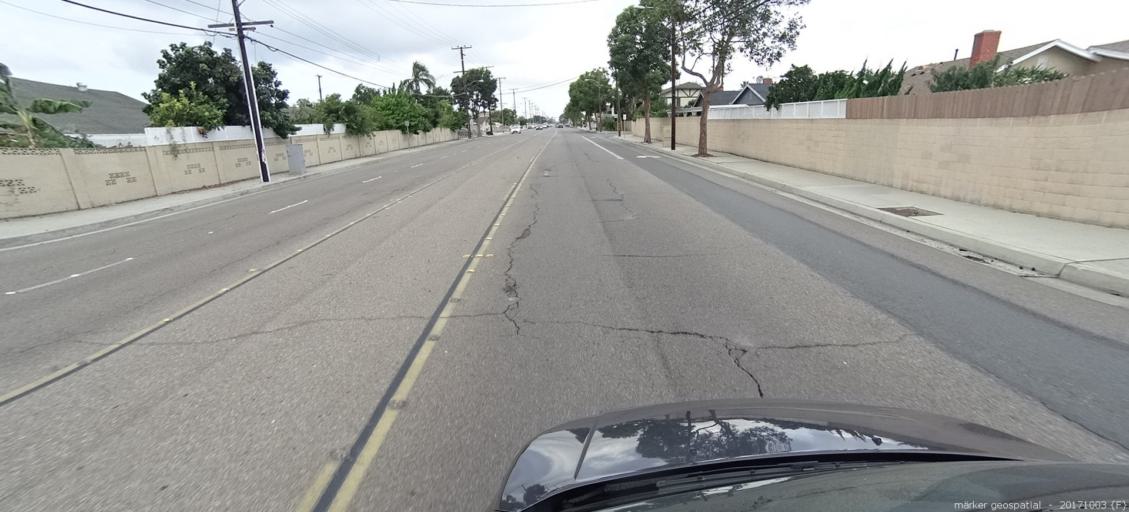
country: US
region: California
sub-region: Orange County
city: Garden Grove
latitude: 33.7522
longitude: -117.9583
